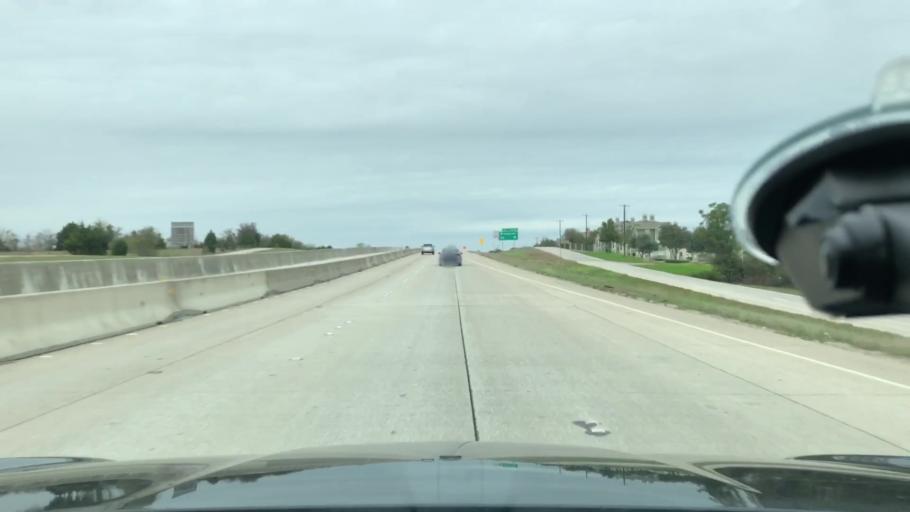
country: US
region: Texas
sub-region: Ellis County
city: Waxahachie
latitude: 32.3882
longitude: -96.8685
